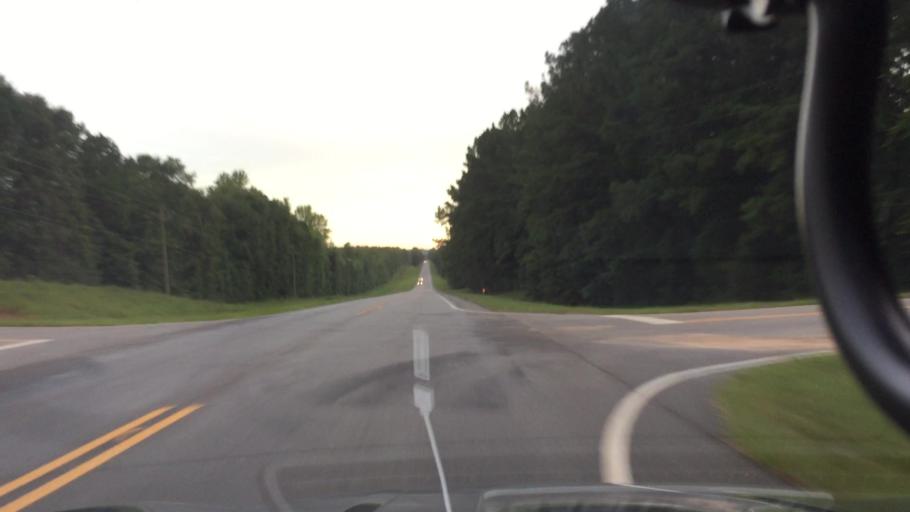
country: US
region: Alabama
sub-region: Coffee County
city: New Brockton
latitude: 31.5161
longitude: -85.9170
